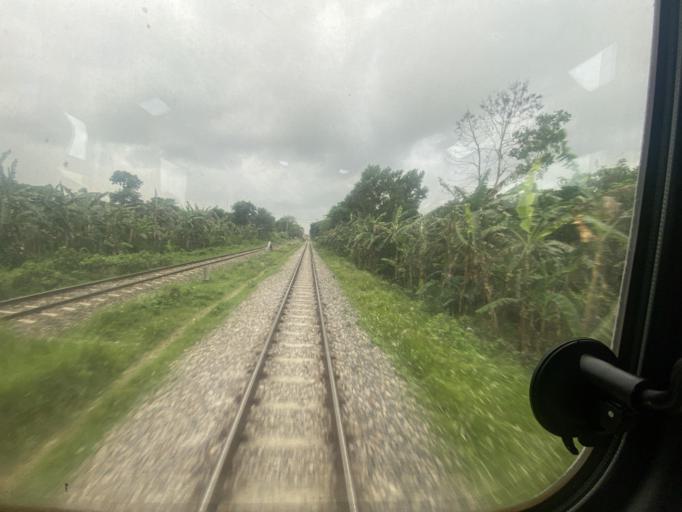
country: BD
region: Dhaka
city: Narsingdi
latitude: 23.9307
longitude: 90.6825
